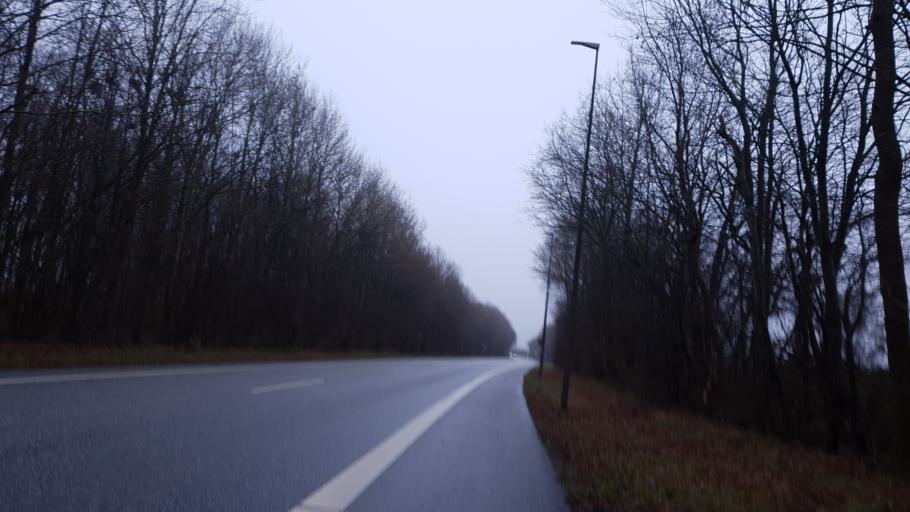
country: DK
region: Central Jutland
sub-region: Hedensted Kommune
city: Hedensted
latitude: 55.7856
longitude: 9.6990
